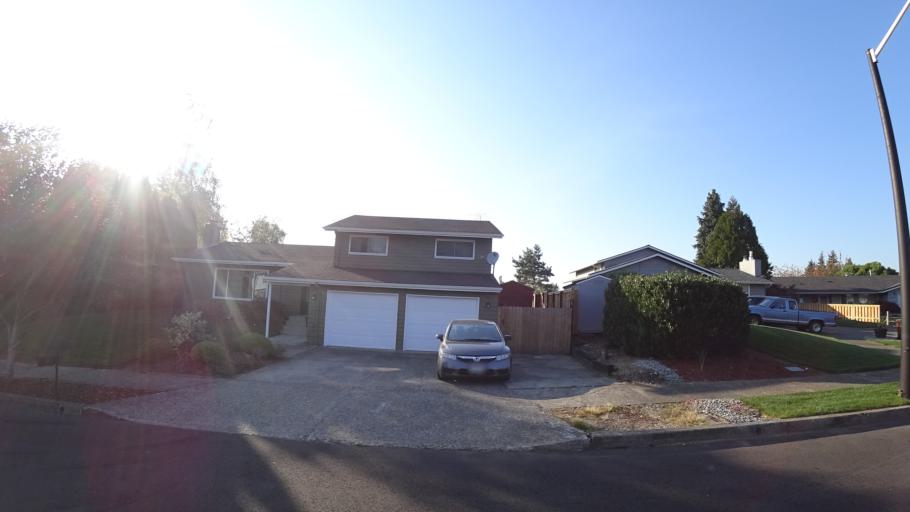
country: US
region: Oregon
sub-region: Multnomah County
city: Gresham
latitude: 45.5075
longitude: -122.4500
